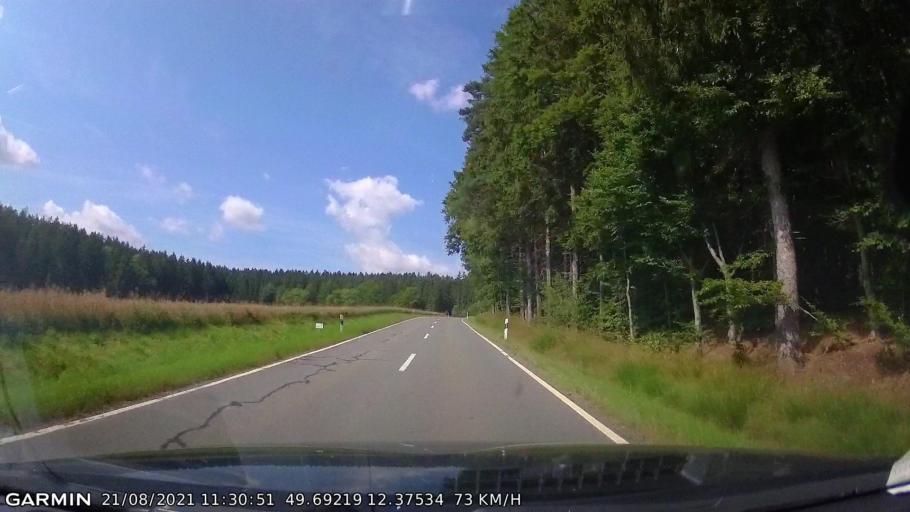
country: DE
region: Bavaria
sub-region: Upper Palatinate
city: Georgenberg
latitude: 49.6922
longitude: 12.3752
